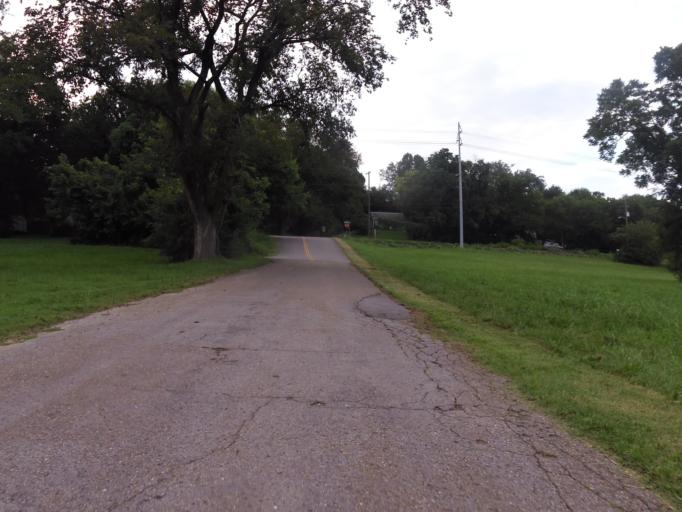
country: US
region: Tennessee
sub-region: Knox County
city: Knoxville
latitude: 35.9680
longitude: -83.8857
